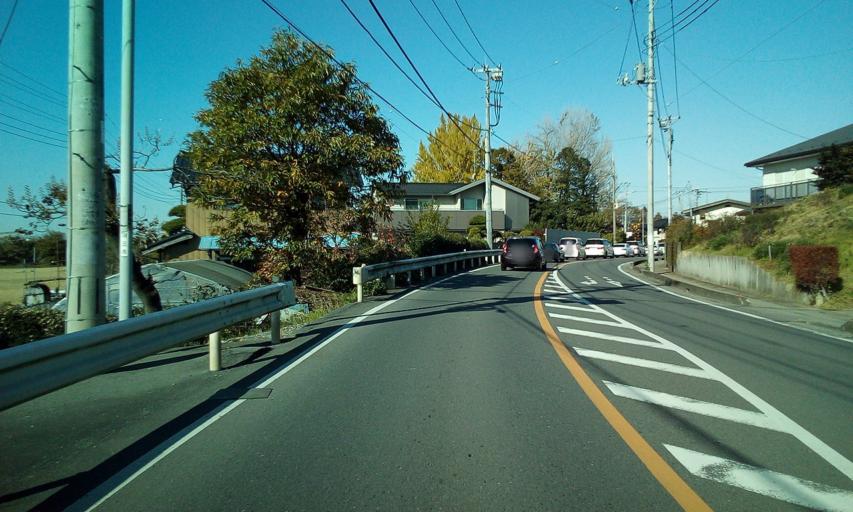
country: JP
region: Saitama
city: Kasukabe
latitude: 35.9788
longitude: 139.7988
